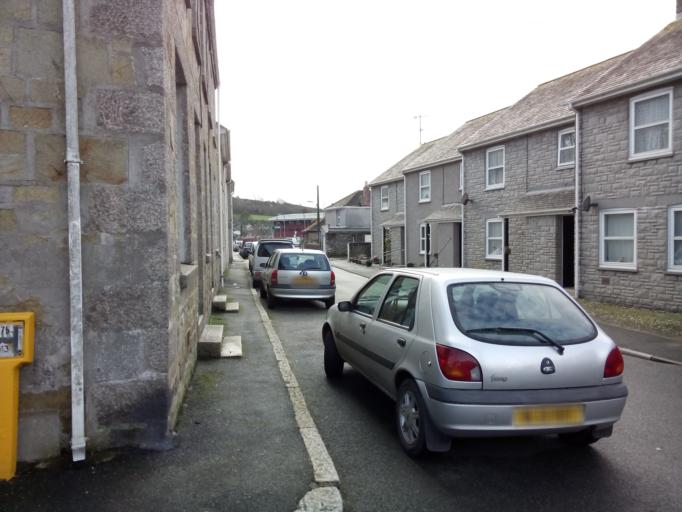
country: GB
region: England
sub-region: Cornwall
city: Helston
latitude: 50.1012
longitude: -5.2789
